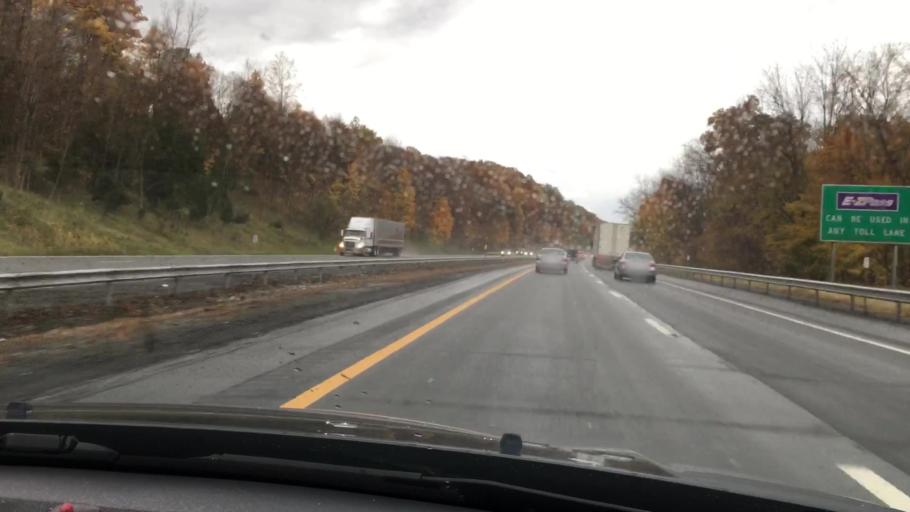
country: US
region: New York
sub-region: Orange County
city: Woodbury
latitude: 41.3570
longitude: -74.1075
